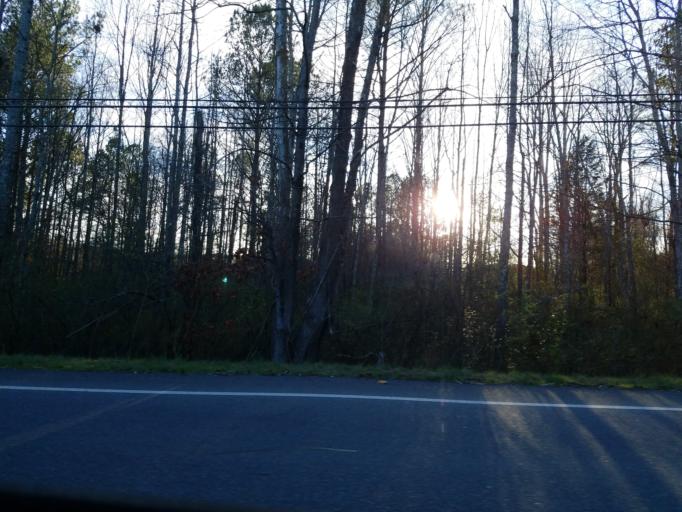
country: US
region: Georgia
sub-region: Gordon County
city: Calhoun
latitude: 34.6267
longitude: -84.9545
